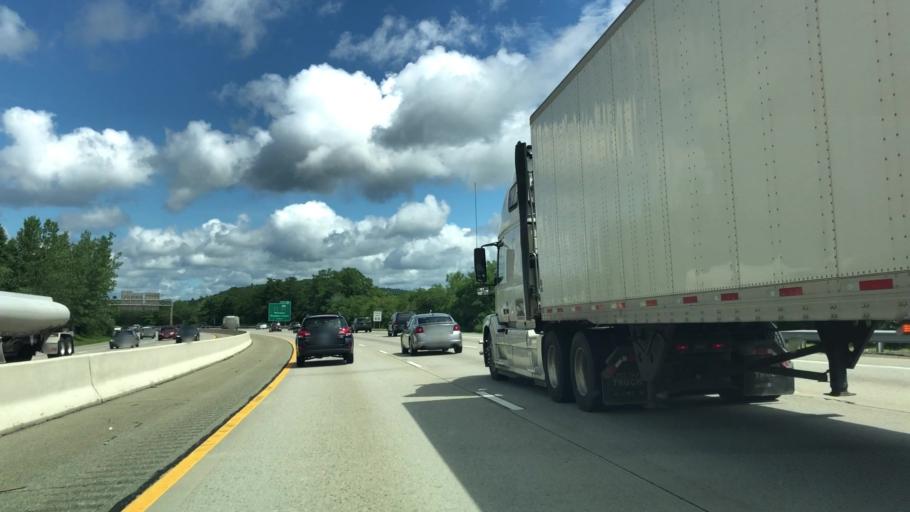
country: US
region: New Jersey
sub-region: Morris County
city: Riverdale
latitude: 41.0023
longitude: -74.3027
